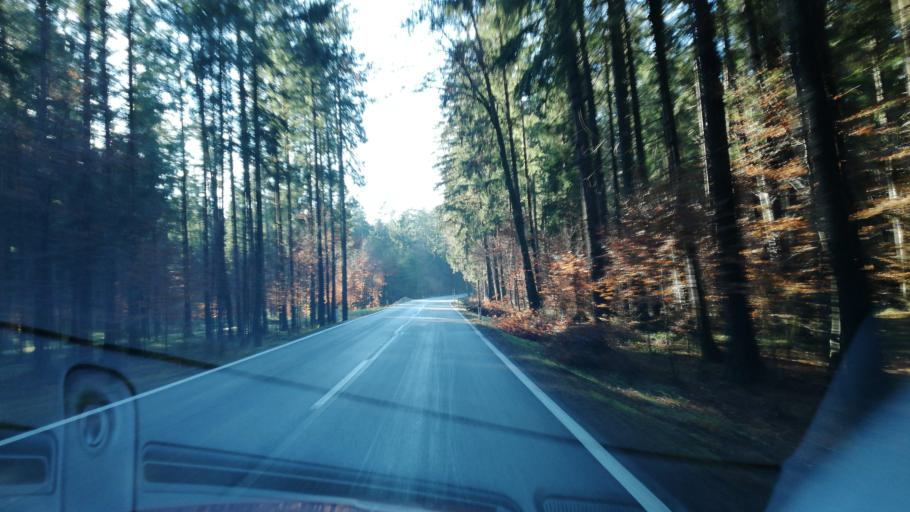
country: DE
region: Bavaria
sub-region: Upper Bavaria
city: Fridolfing
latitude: 48.0642
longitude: 12.8851
